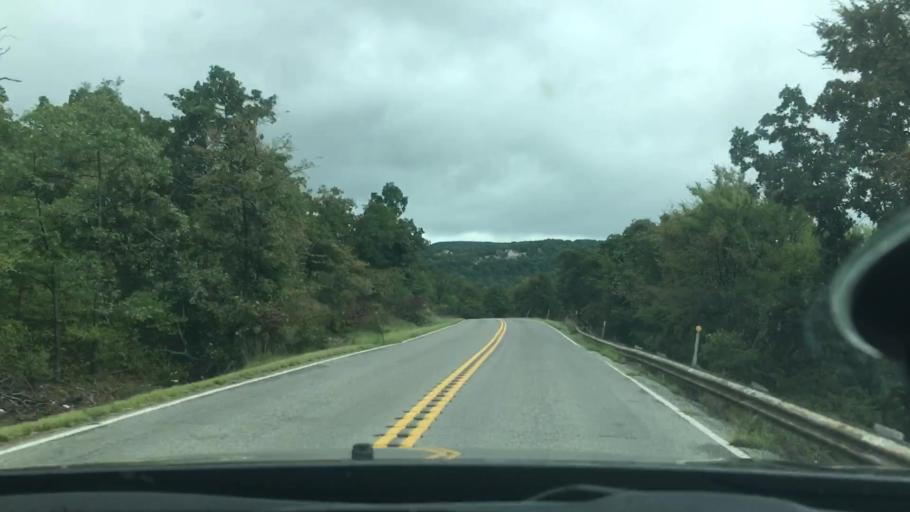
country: US
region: Oklahoma
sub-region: Sequoyah County
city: Vian
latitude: 35.6294
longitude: -94.9645
